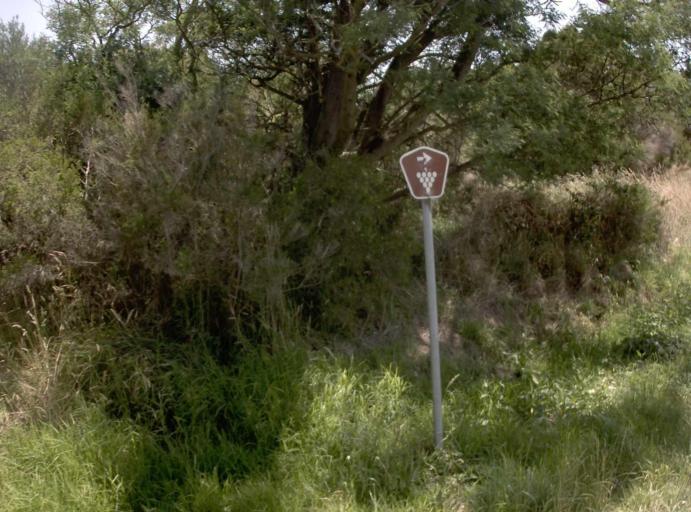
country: AU
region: Victoria
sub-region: Bass Coast
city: North Wonthaggi
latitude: -38.6624
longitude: 145.9293
